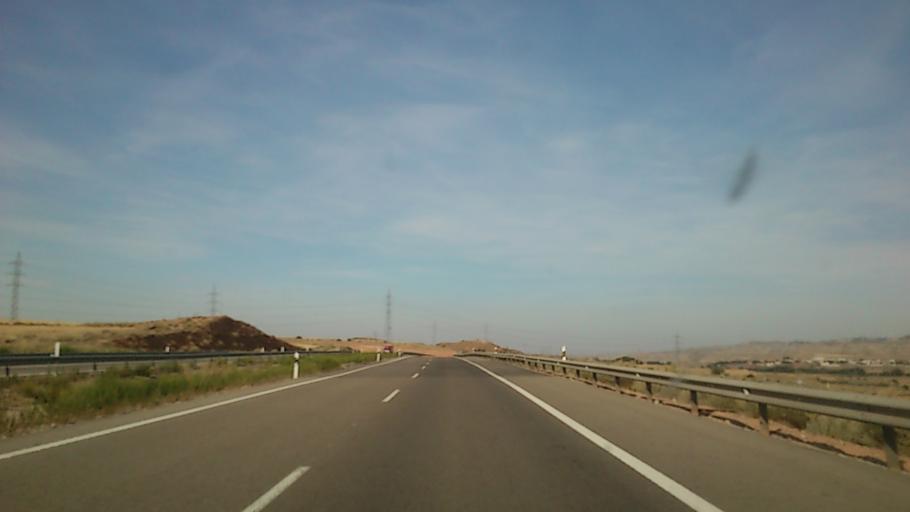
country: ES
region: Aragon
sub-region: Provincia de Zaragoza
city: Mozota
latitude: 41.4952
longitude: -1.0662
